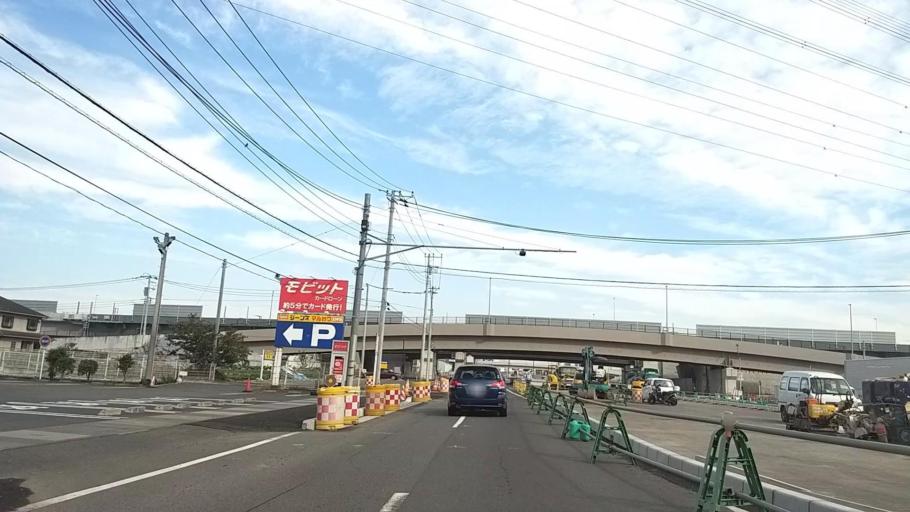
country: JP
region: Kanagawa
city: Atsugi
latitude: 35.4051
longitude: 139.3615
